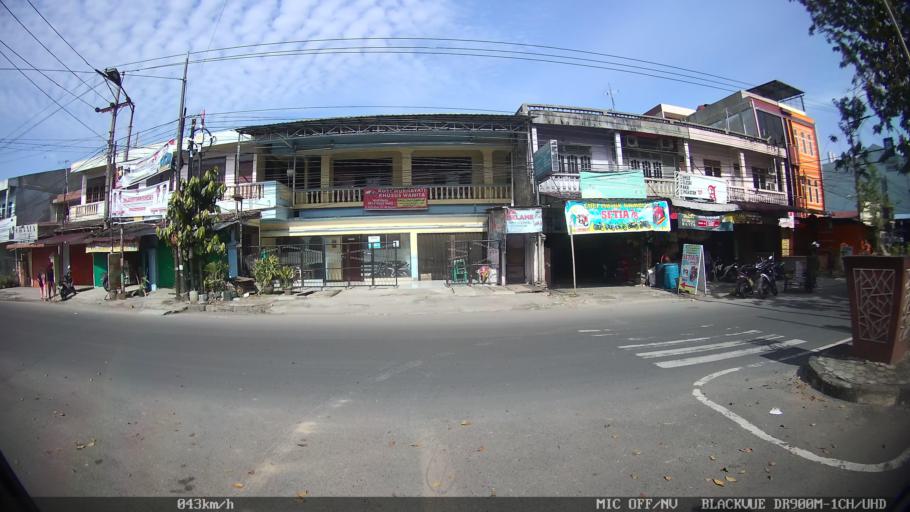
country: ID
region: North Sumatra
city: Medan
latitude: 3.5785
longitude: 98.6431
